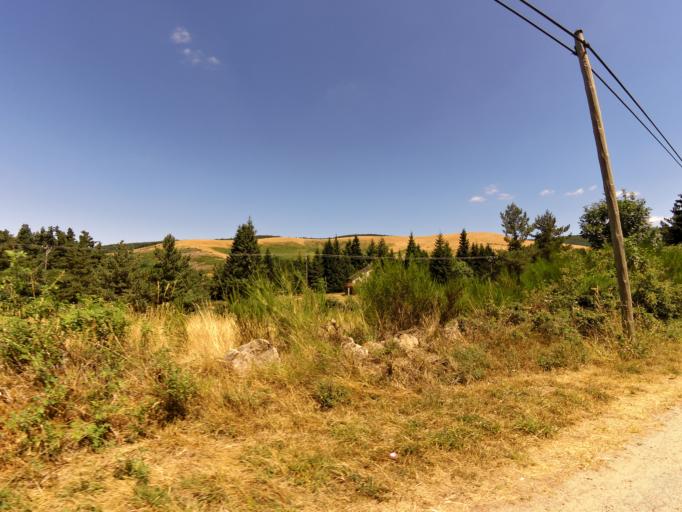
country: FR
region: Languedoc-Roussillon
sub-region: Departement de la Lozere
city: Meyrueis
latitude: 44.1145
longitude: 3.4893
